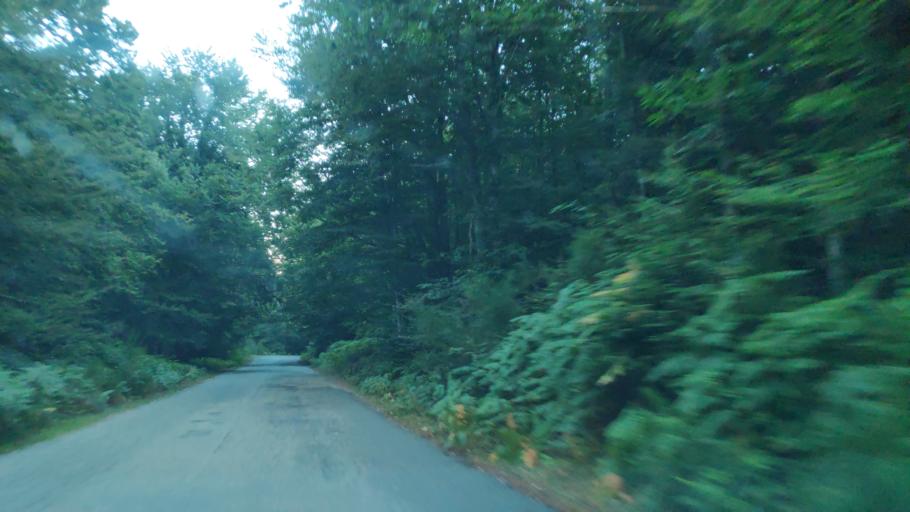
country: IT
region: Calabria
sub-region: Provincia di Vibo-Valentia
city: Nardodipace
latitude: 38.4930
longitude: 16.3611
